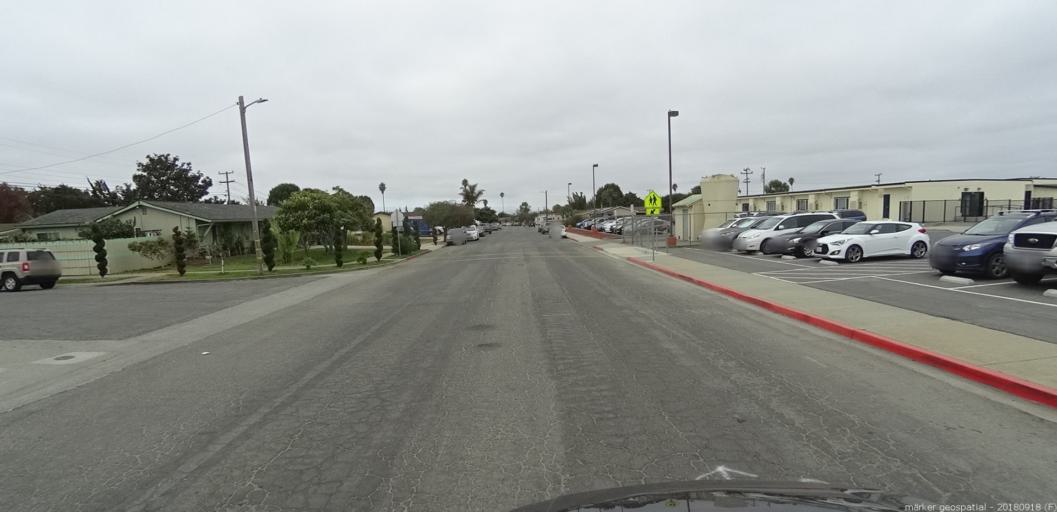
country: US
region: California
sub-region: Monterey County
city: Boronda
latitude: 36.7323
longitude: -121.6340
